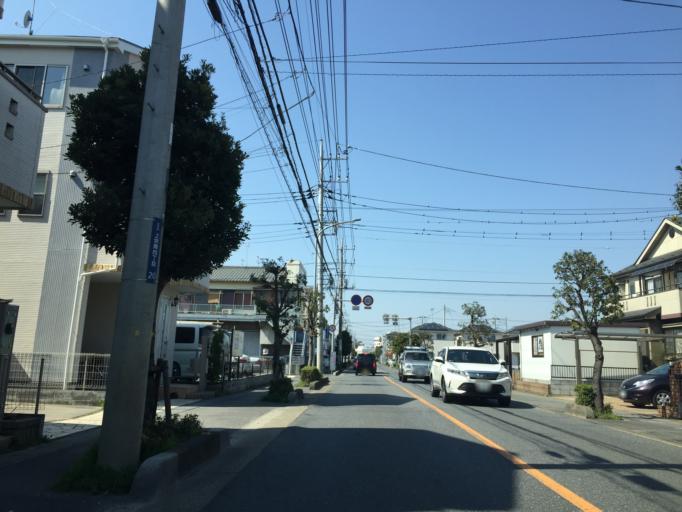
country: JP
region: Saitama
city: Shiki
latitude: 35.8470
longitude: 139.5893
